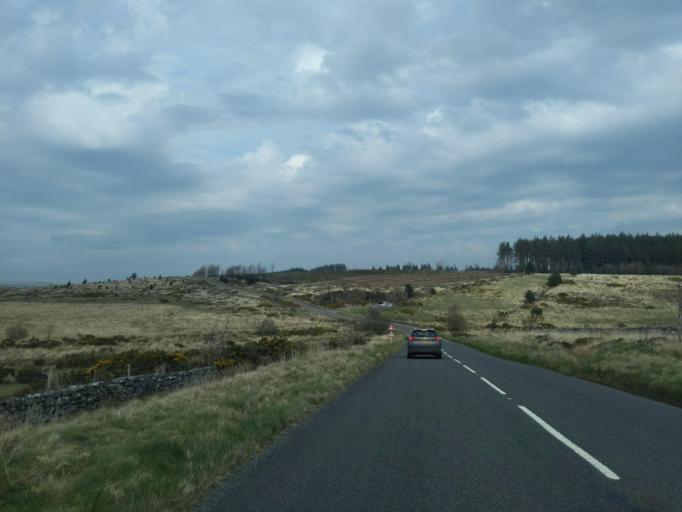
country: GB
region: England
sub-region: Devon
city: Yelverton
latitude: 50.5756
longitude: -3.9322
